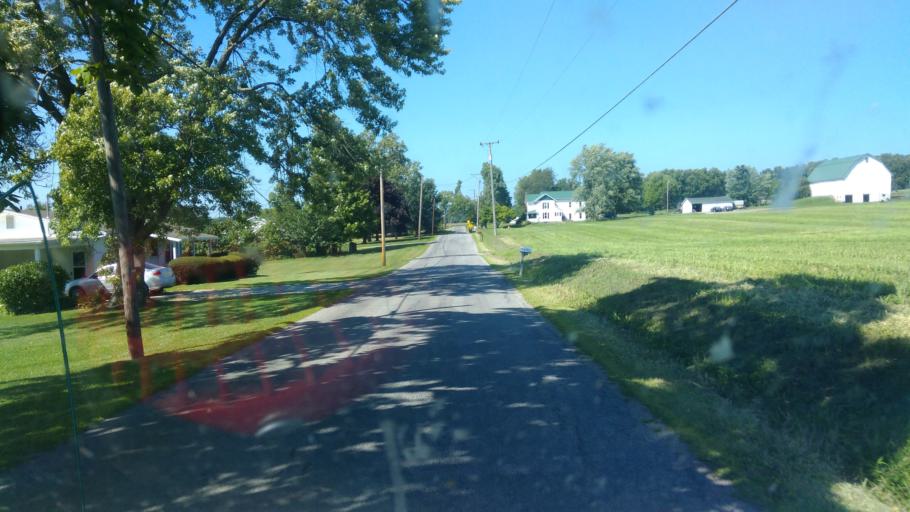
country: US
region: Ohio
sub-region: Ashland County
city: Ashland
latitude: 40.8971
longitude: -82.2686
